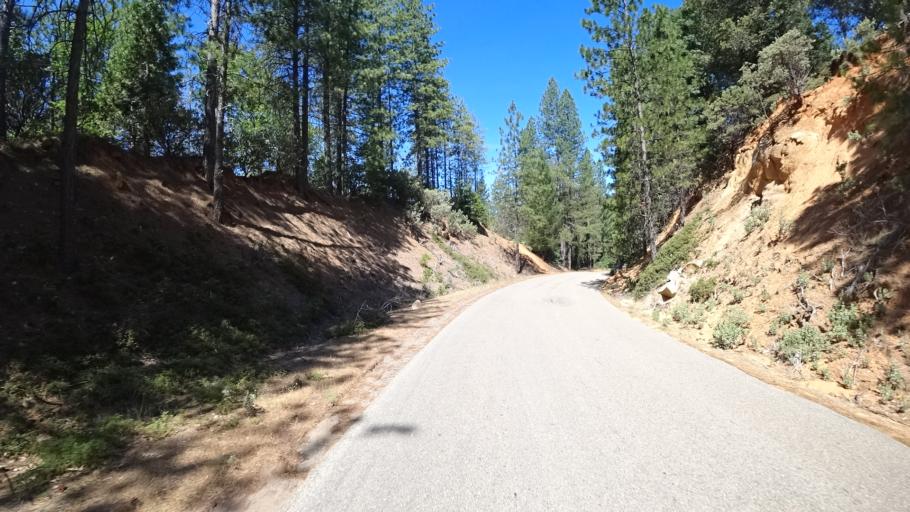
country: US
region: California
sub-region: Amador County
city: Pioneer
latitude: 38.4251
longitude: -120.4842
